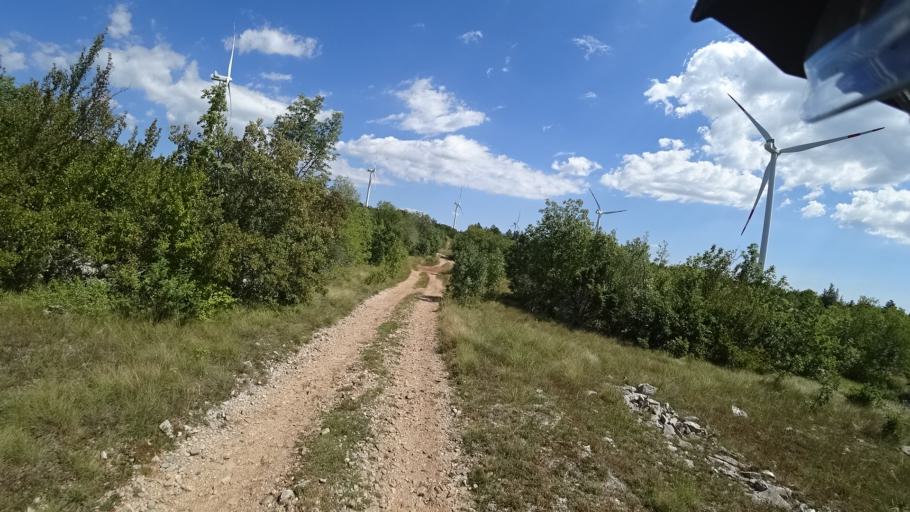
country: HR
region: Splitsko-Dalmatinska
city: Hrvace
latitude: 43.7182
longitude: 16.5167
